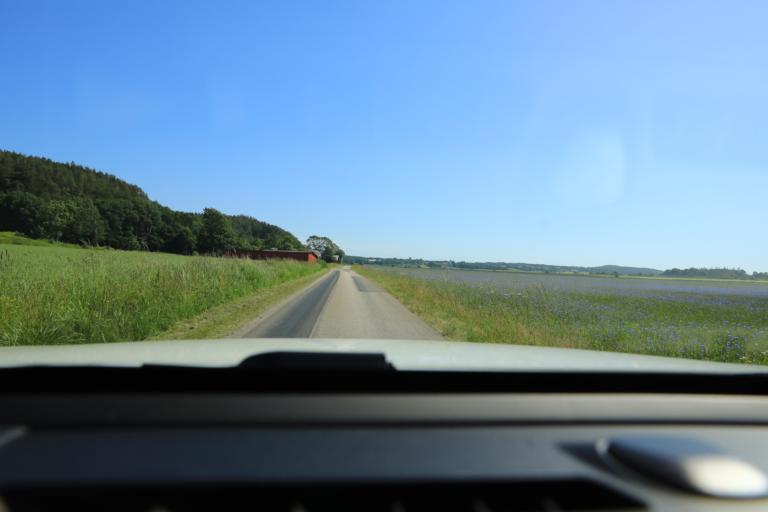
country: SE
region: Halland
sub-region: Varbergs Kommun
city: Veddige
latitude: 57.1822
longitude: 12.3148
